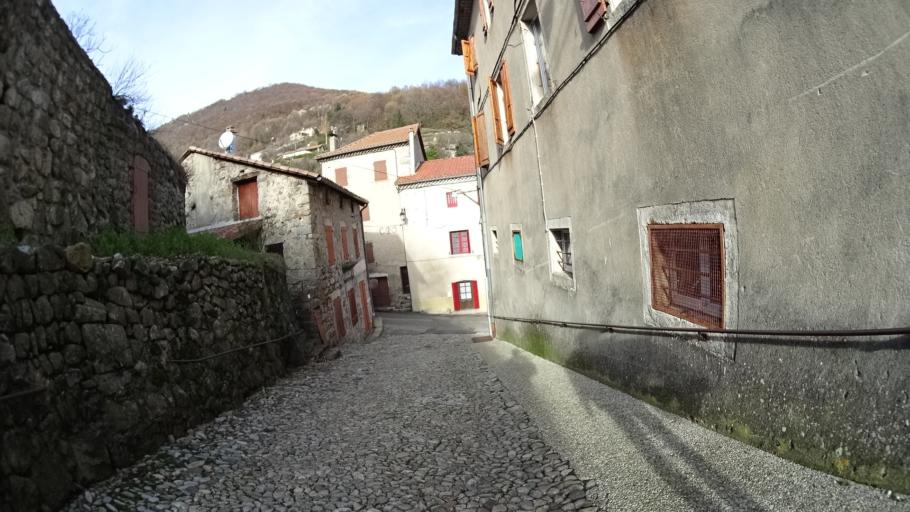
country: FR
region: Rhone-Alpes
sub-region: Departement de l'Ardeche
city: Thueyts
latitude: 44.7407
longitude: 4.2409
